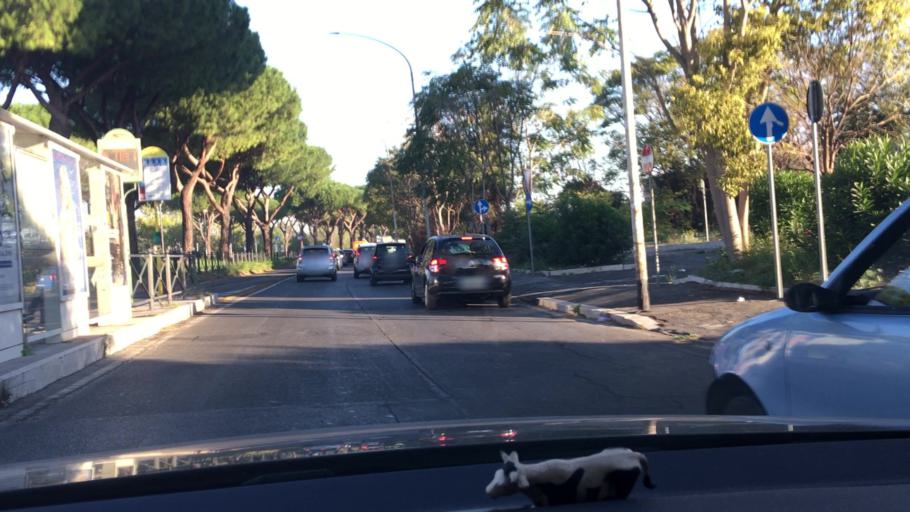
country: IT
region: Latium
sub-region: Citta metropolitana di Roma Capitale
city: Rome
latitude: 41.8648
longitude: 12.5682
